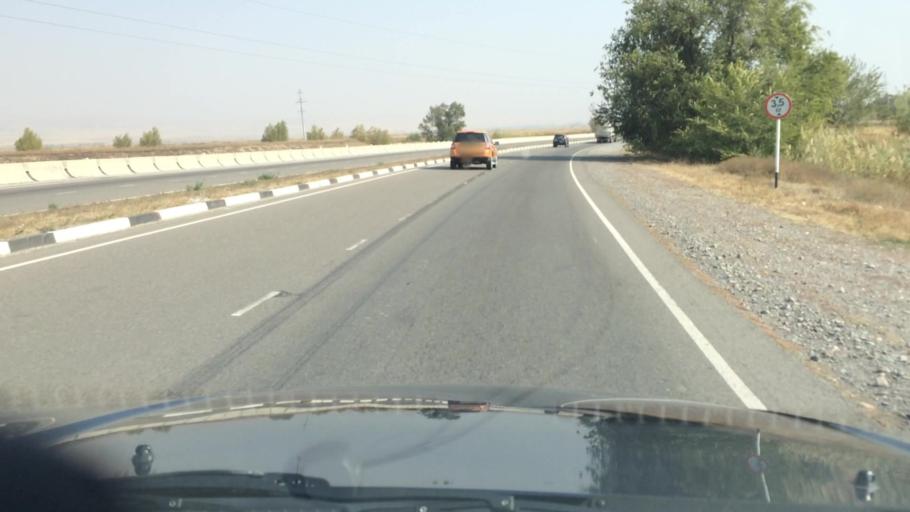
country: KG
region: Chuy
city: Kant
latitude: 42.9640
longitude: 74.8083
